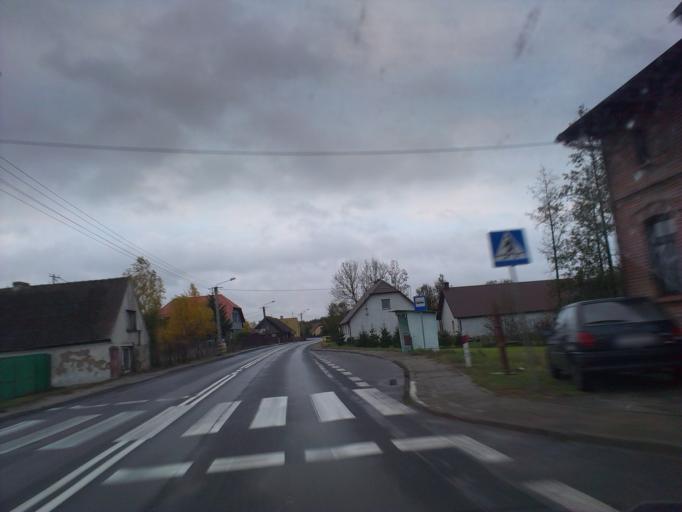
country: PL
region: Kujawsko-Pomorskie
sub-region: Powiat tucholski
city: Cekcyn
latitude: 53.5328
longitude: 17.9442
